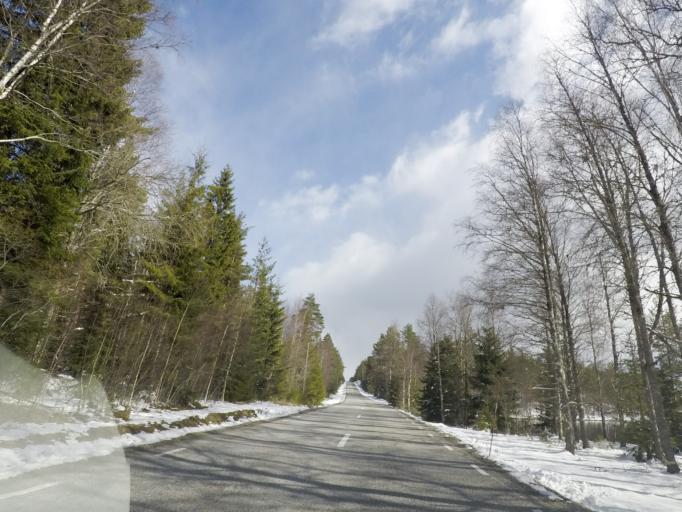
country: SE
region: OErebro
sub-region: Lindesbergs Kommun
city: Stora
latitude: 59.8997
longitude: 15.2162
